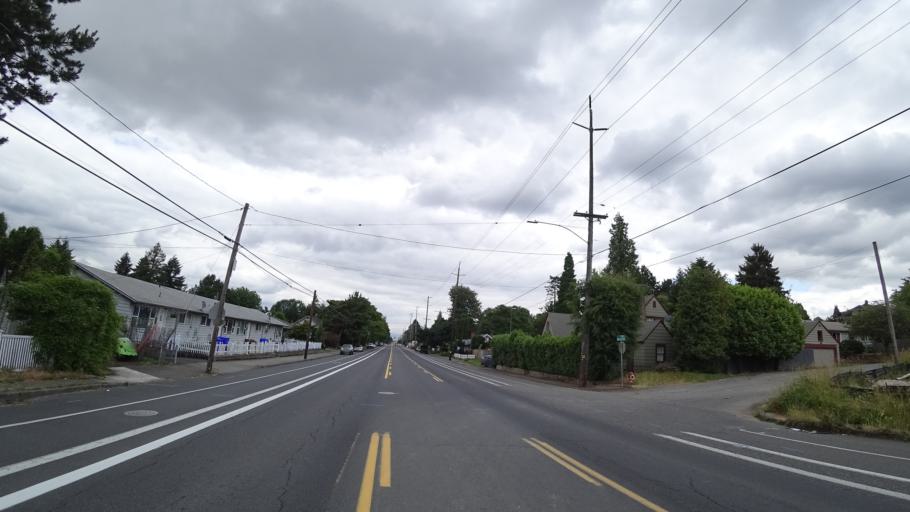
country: US
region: Oregon
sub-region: Multnomah County
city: Portland
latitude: 45.5628
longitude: -122.6046
